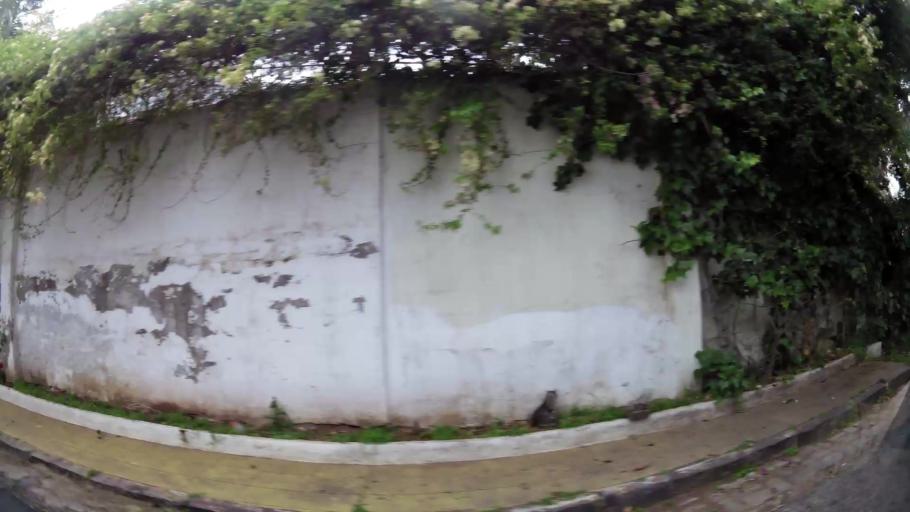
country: MA
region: Grand Casablanca
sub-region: Casablanca
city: Casablanca
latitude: 33.5628
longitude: -7.6350
